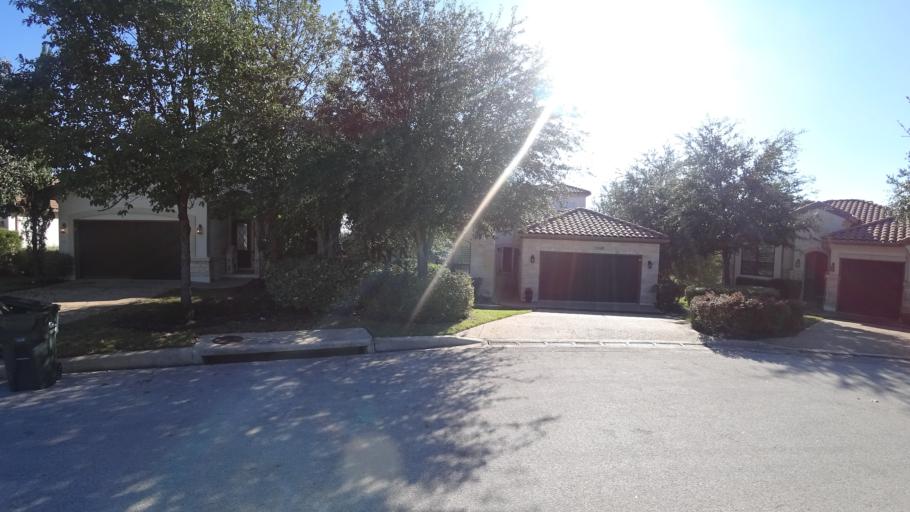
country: US
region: Texas
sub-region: Travis County
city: Bee Cave
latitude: 30.3496
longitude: -97.8927
